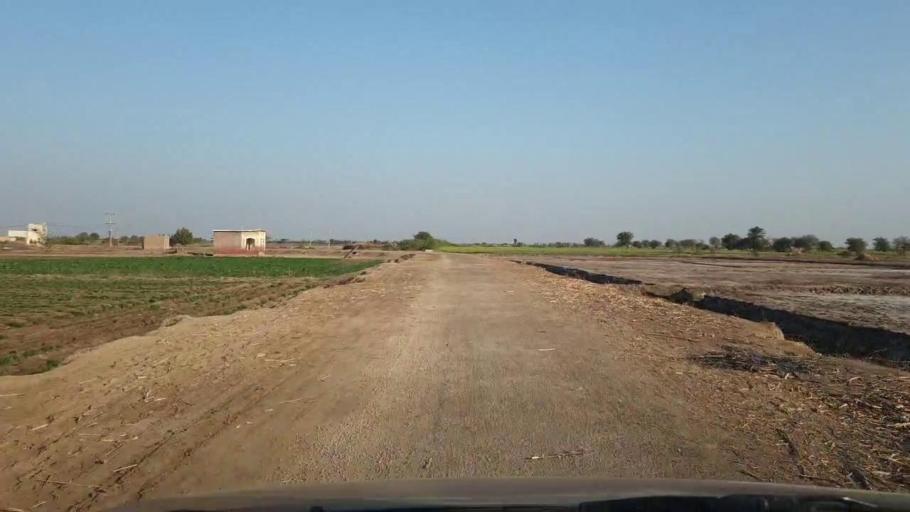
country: PK
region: Sindh
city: Samaro
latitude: 25.1389
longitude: 69.3045
